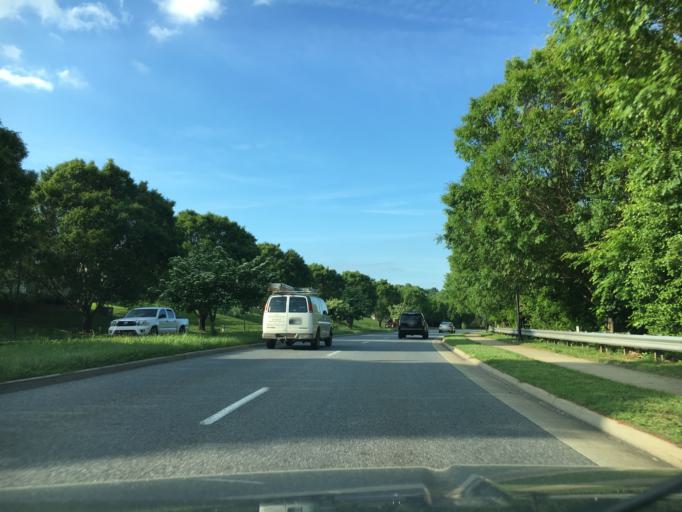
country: US
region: Virginia
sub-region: Campbell County
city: Timberlake
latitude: 37.3540
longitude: -79.2409
